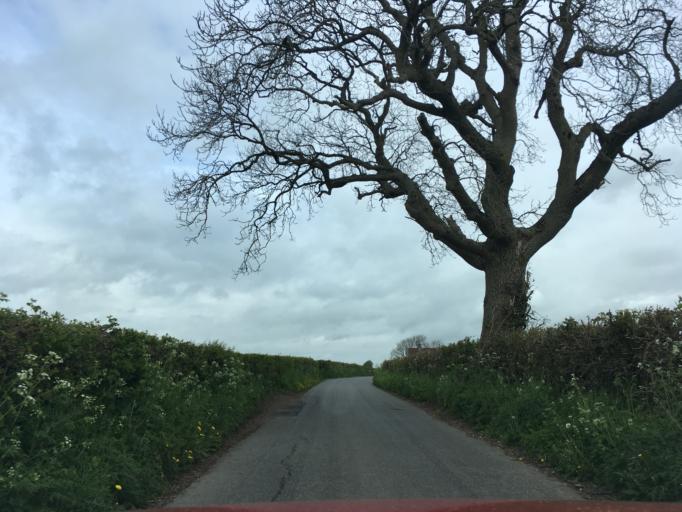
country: GB
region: England
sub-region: Bath and North East Somerset
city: Clutton
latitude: 51.3325
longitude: -2.5183
